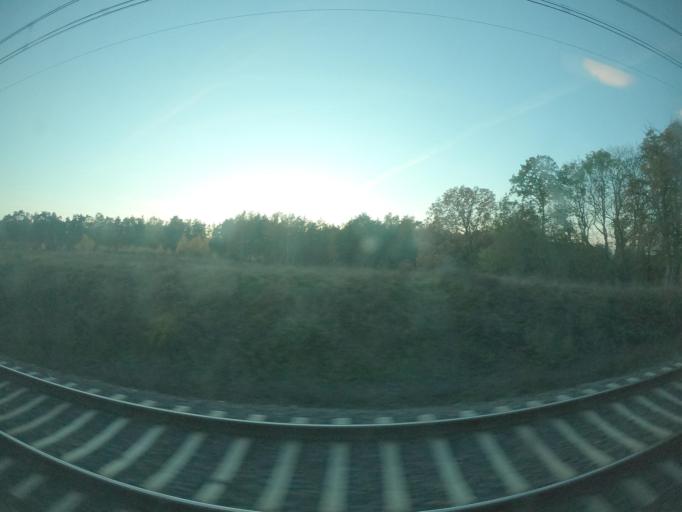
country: PL
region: West Pomeranian Voivodeship
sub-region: Powiat mysliborski
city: Boleszkowice
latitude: 52.7264
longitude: 14.5248
